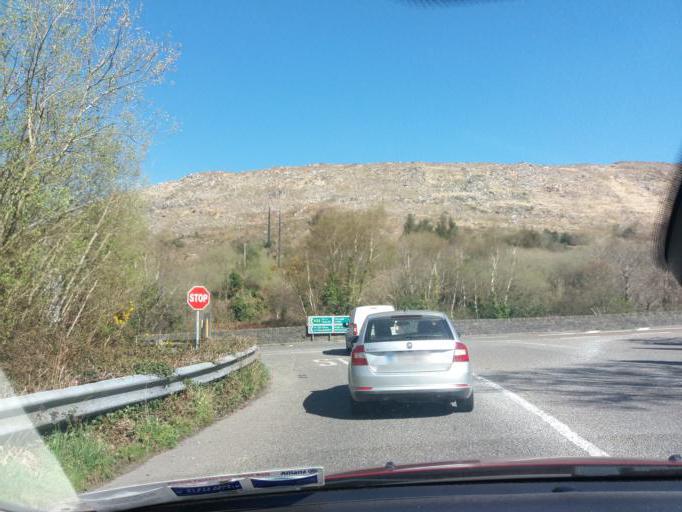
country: IE
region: Munster
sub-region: Ciarrai
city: Cill Airne
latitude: 51.9818
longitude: -9.3140
